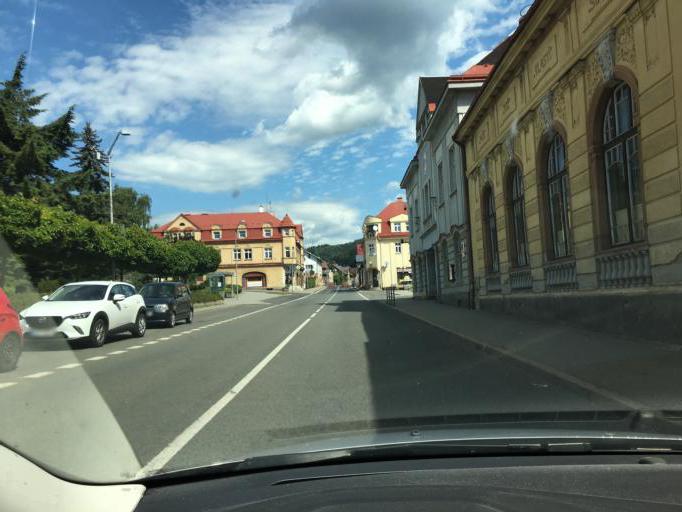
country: CZ
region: Liberecky
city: Velke Hamry
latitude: 50.7170
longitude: 15.3148
